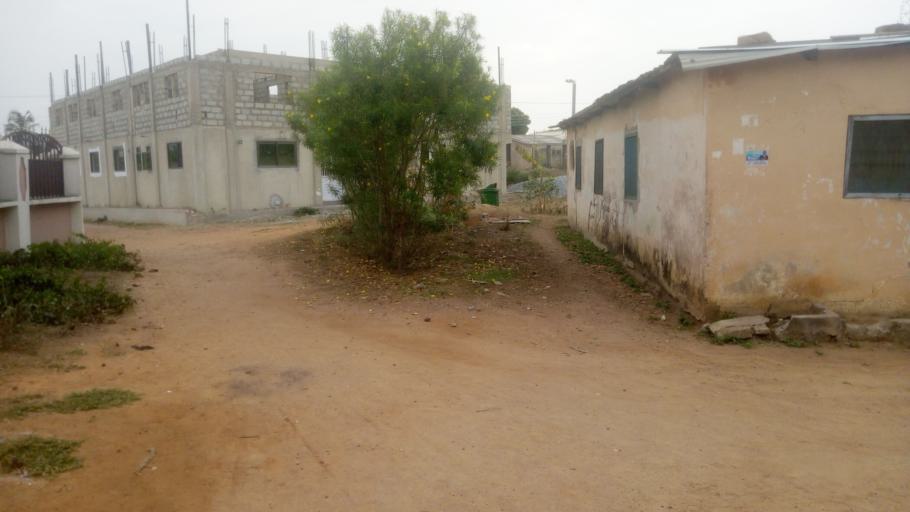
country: GH
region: Central
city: Winneba
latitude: 5.3607
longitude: -0.6278
